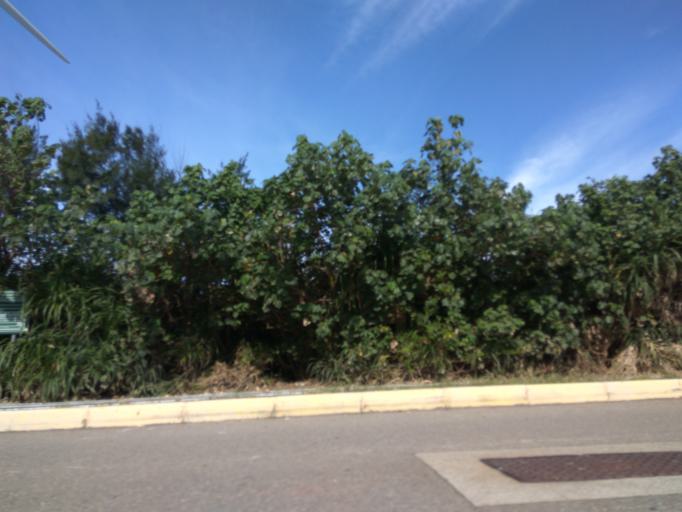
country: TW
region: Taiwan
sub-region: Hsinchu
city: Zhubei
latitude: 25.0444
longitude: 121.0738
